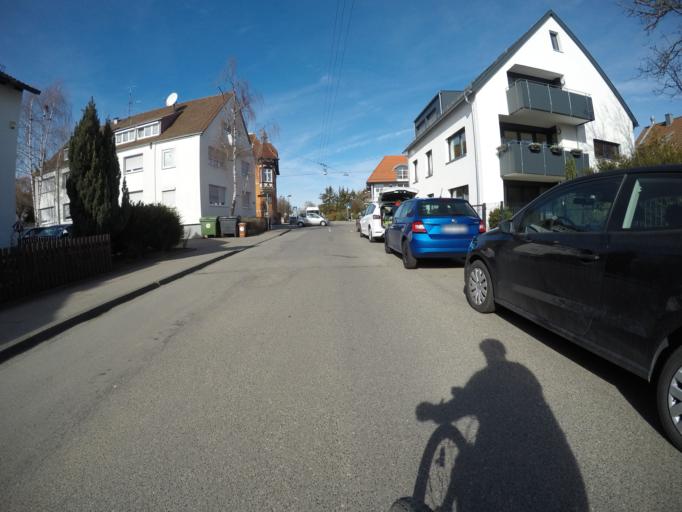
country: DE
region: Baden-Wuerttemberg
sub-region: Regierungsbezirk Stuttgart
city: Leinfelden-Echterdingen
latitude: 48.7287
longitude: 9.1444
